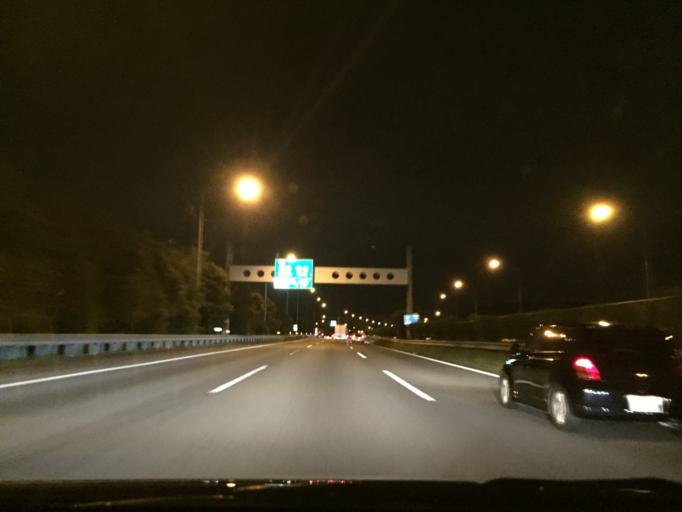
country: JP
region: Kanagawa
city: Hadano
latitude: 35.3542
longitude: 139.2387
